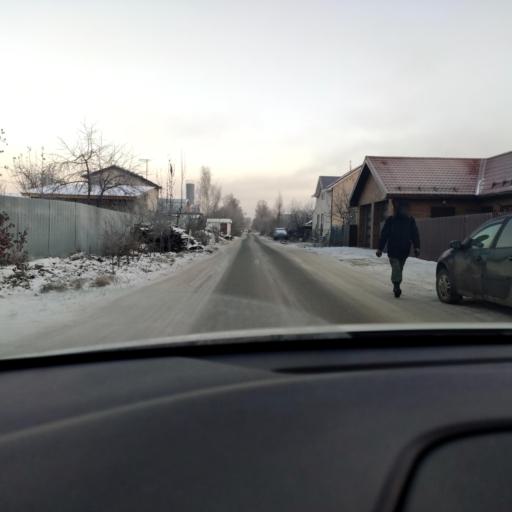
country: RU
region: Tatarstan
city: Staroye Arakchino
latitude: 55.8621
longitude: 49.0467
